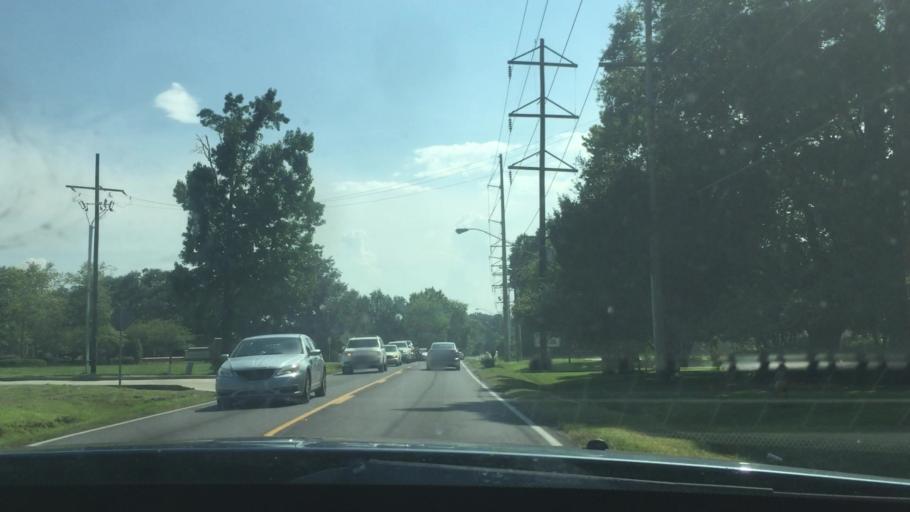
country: US
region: Louisiana
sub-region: East Baton Rouge Parish
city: Monticello
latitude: 30.4448
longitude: -91.0354
